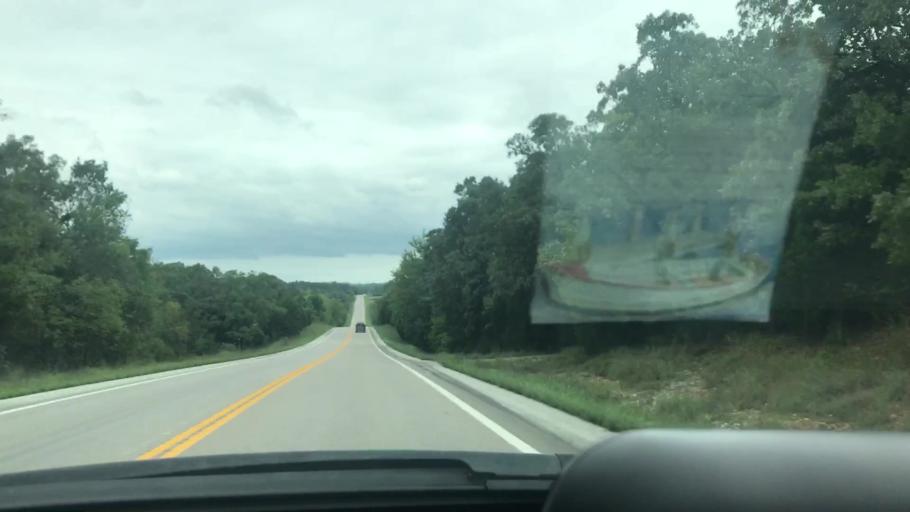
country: US
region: Missouri
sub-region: Dallas County
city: Buffalo
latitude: 37.7136
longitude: -93.1170
